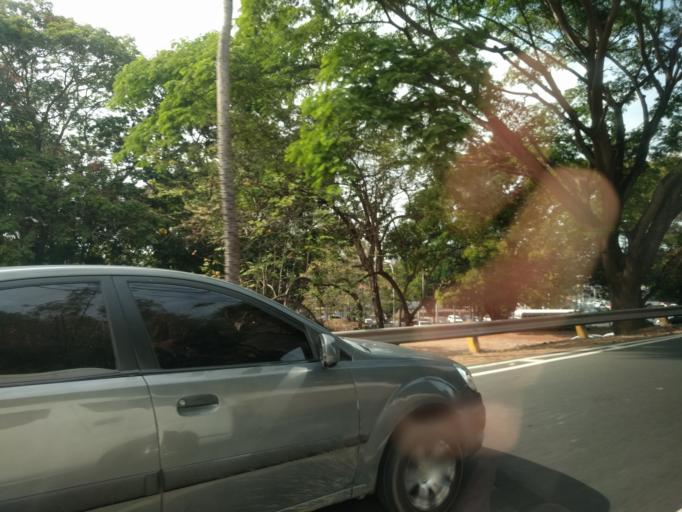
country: PA
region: Panama
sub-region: Distrito de Panama
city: Ancon
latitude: 8.9648
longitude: -79.5525
